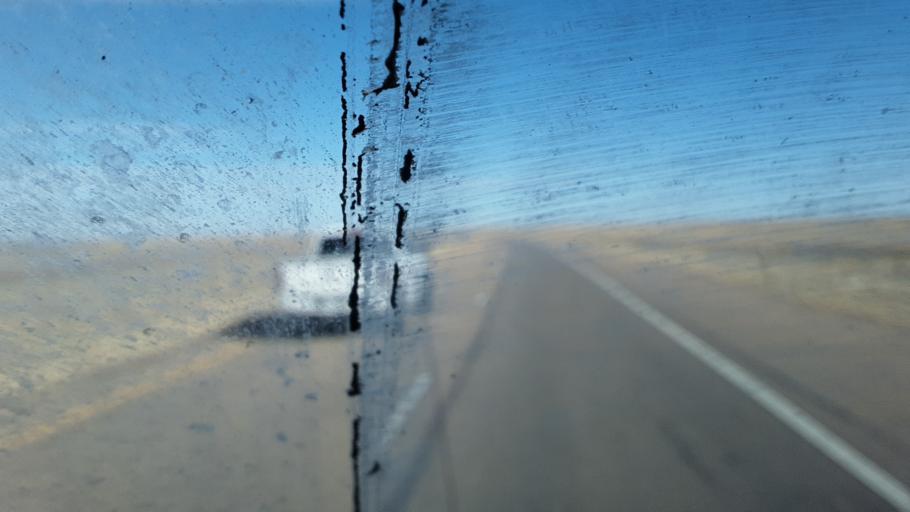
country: US
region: Colorado
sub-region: Weld County
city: Keenesburg
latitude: 40.1715
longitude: -104.3422
